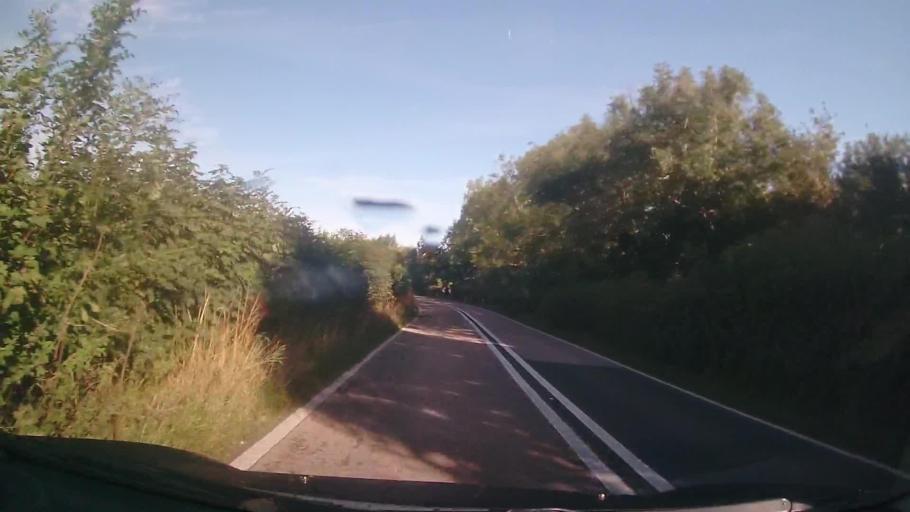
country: GB
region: Wales
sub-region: Sir Powys
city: Hay
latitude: 51.9660
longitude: -3.2100
